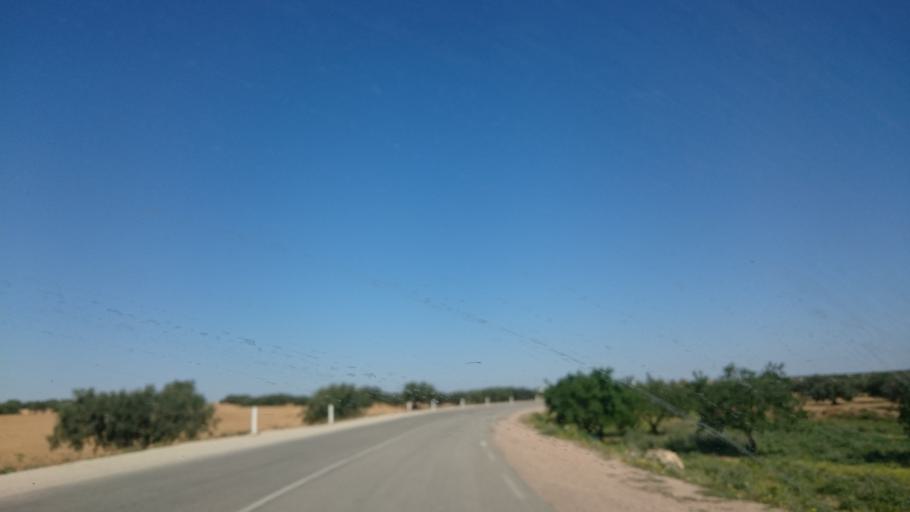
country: TN
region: Safaqis
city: Sfax
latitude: 34.7513
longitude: 10.5235
